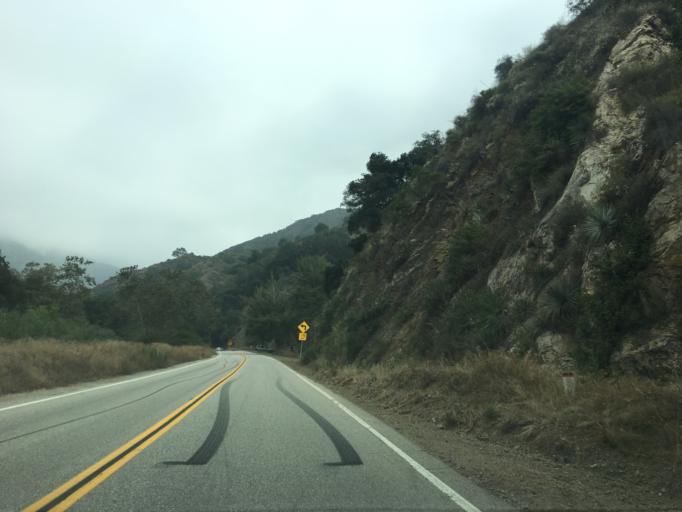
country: US
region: California
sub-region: Los Angeles County
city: Glendora
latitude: 34.1652
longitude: -117.8387
